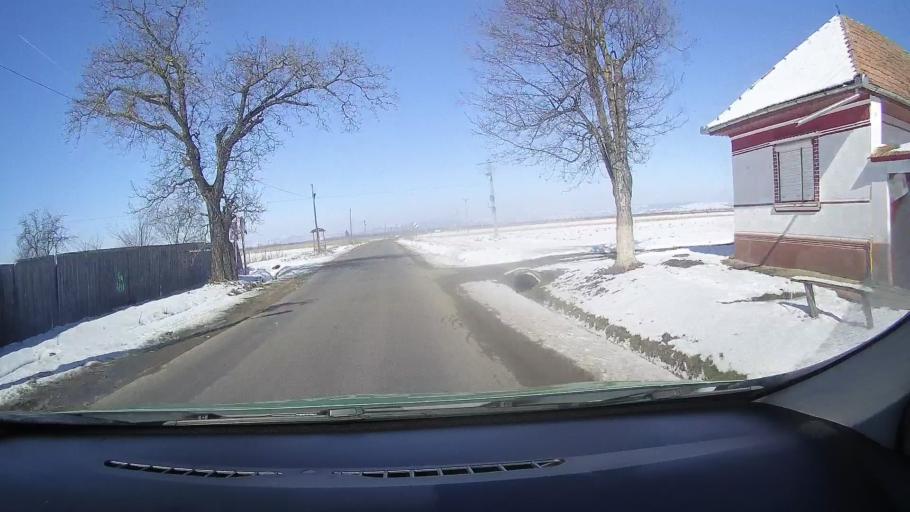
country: RO
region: Brasov
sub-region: Comuna Harseni
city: Harseni
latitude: 45.7593
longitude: 25.0091
